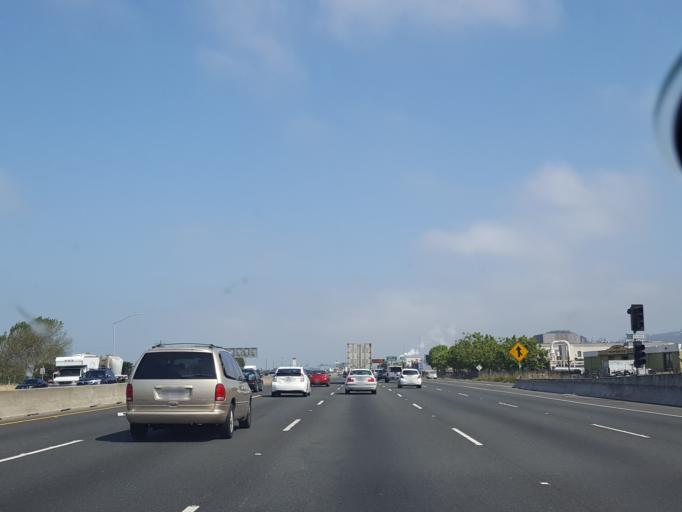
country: US
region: California
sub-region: Alameda County
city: Albany
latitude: 37.8675
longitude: -122.3038
